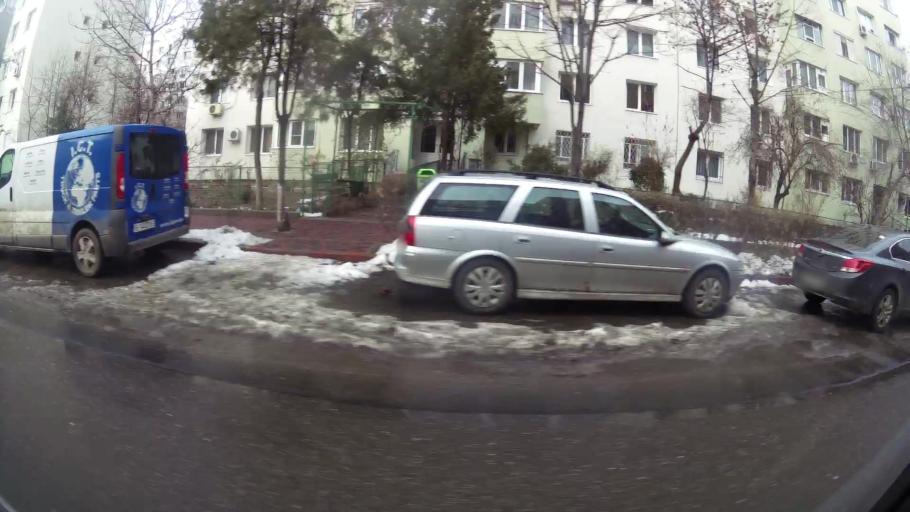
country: RO
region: Ilfov
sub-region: Comuna Popesti-Leordeni
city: Popesti-Leordeni
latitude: 44.4096
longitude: 26.1666
